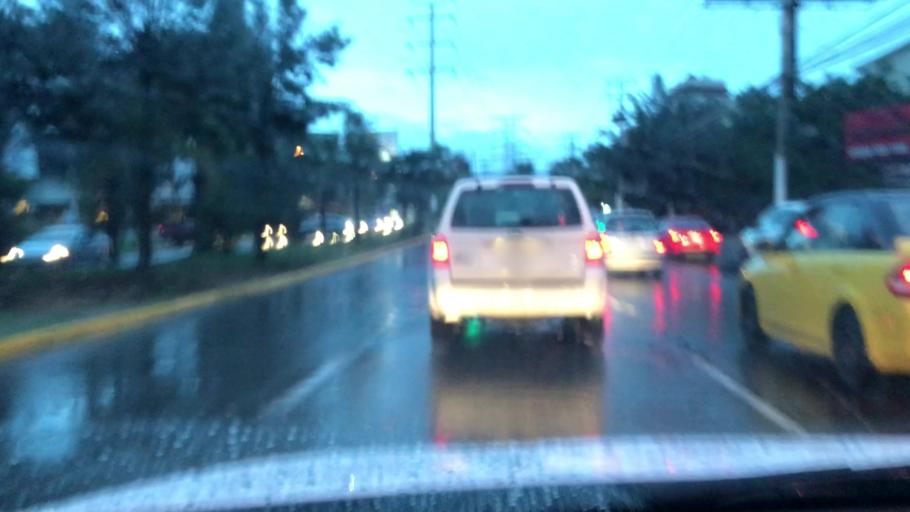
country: MX
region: Jalisco
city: Guadalajara
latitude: 20.6863
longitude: -103.4202
